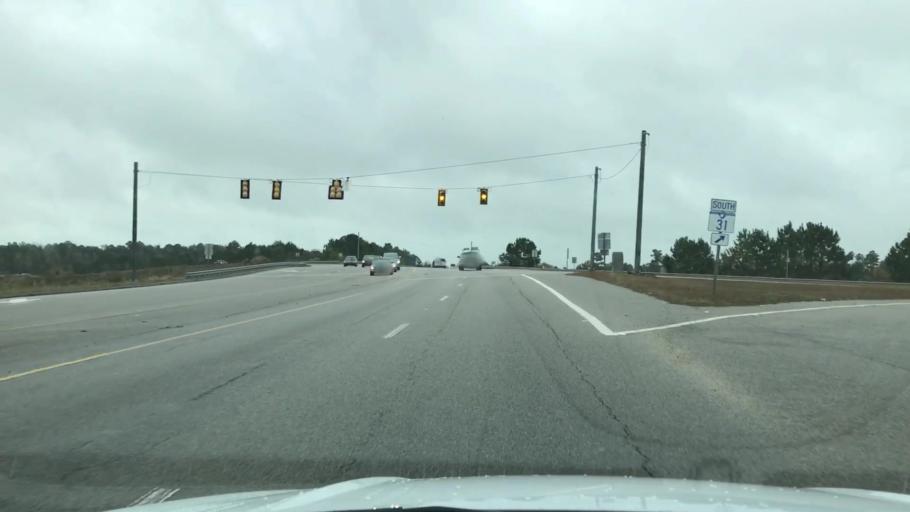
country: US
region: South Carolina
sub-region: Horry County
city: Myrtle Beach
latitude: 33.7566
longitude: -78.8553
